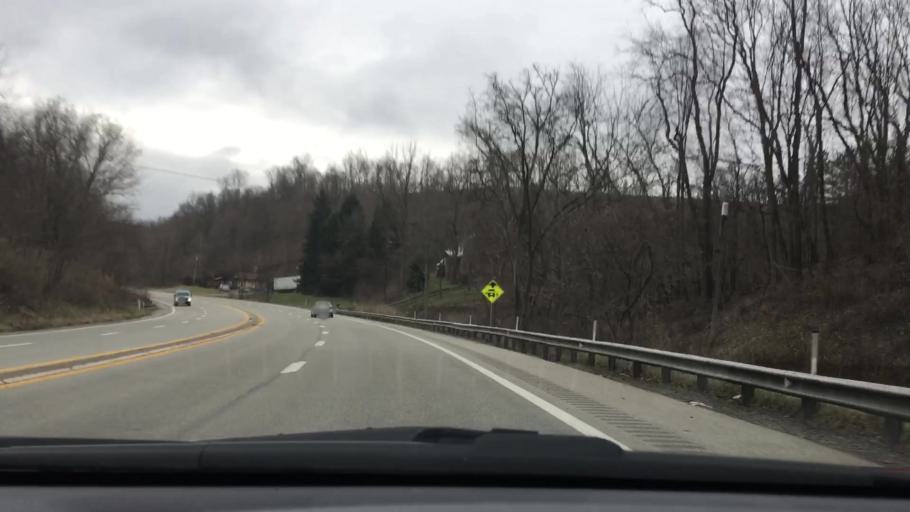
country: US
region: Pennsylvania
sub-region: Fayette County
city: Perryopolis
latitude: 40.0136
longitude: -79.7662
